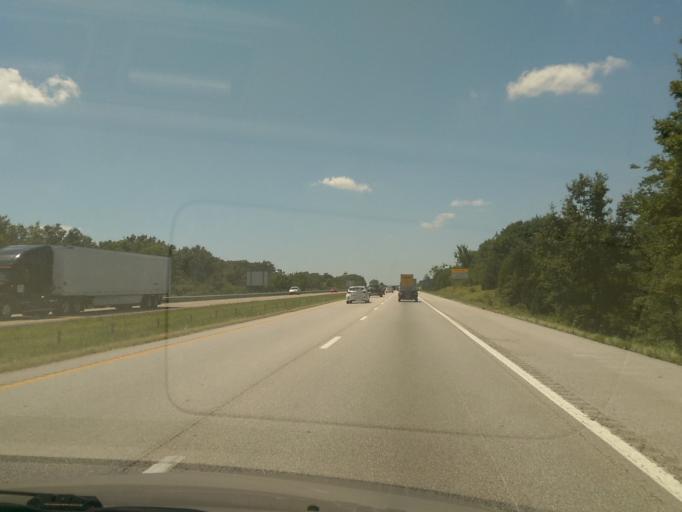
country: US
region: Missouri
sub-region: Cooper County
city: Boonville
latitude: 38.9361
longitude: -92.7643
